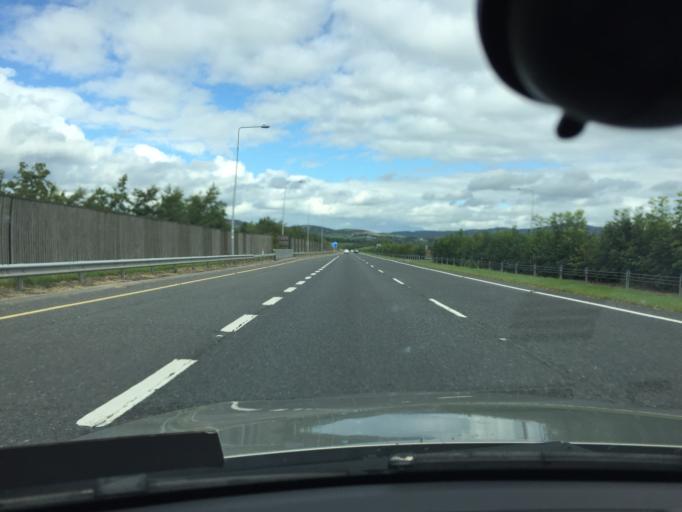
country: IE
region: Leinster
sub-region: Lu
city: Dundalk
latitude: 54.0232
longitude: -6.4394
